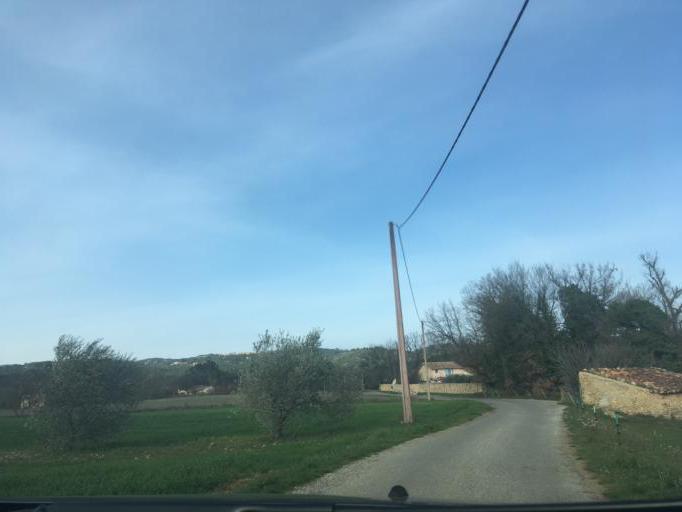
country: FR
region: Provence-Alpes-Cote d'Azur
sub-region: Departement du Var
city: Villecroze
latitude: 43.5626
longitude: 6.2819
